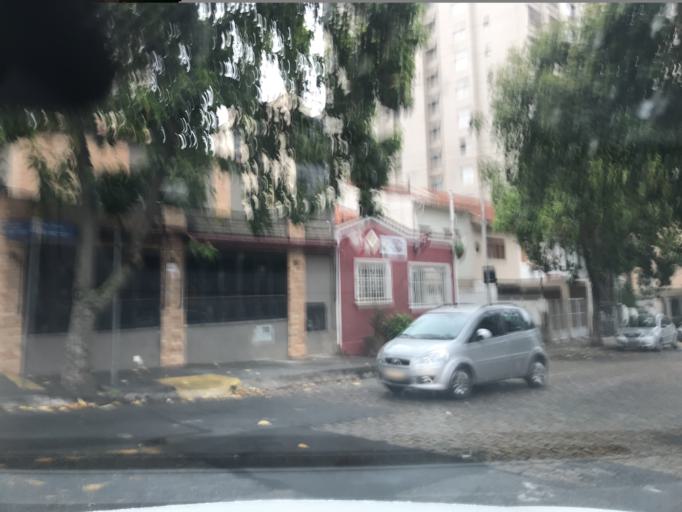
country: BR
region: Sao Paulo
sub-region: Sao Paulo
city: Sao Paulo
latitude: -23.5313
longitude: -46.6827
